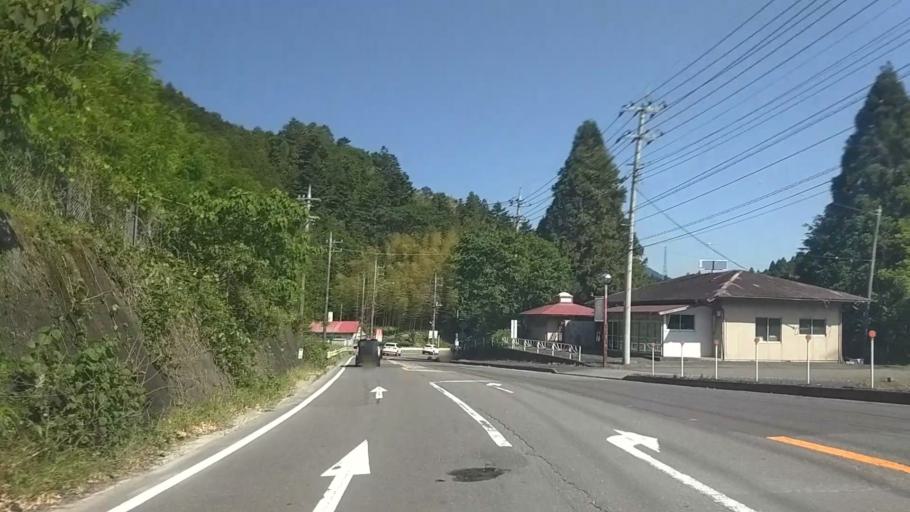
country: JP
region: Shizuoka
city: Fujinomiya
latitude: 35.2748
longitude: 138.4511
